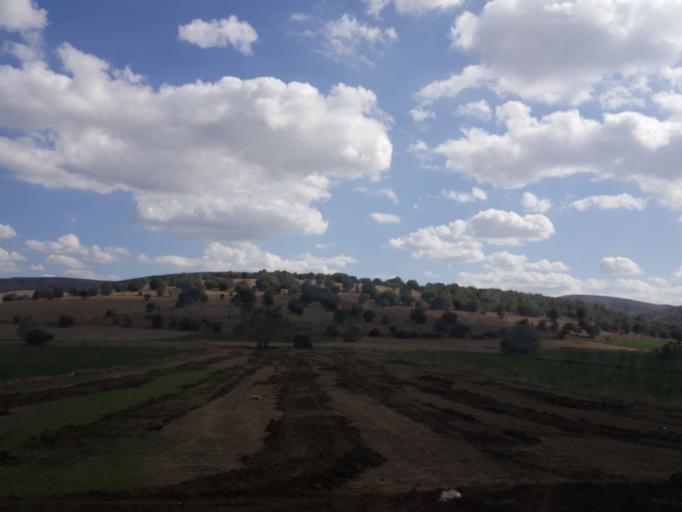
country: TR
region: Tokat
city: Camlibel
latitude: 40.1634
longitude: 36.4211
